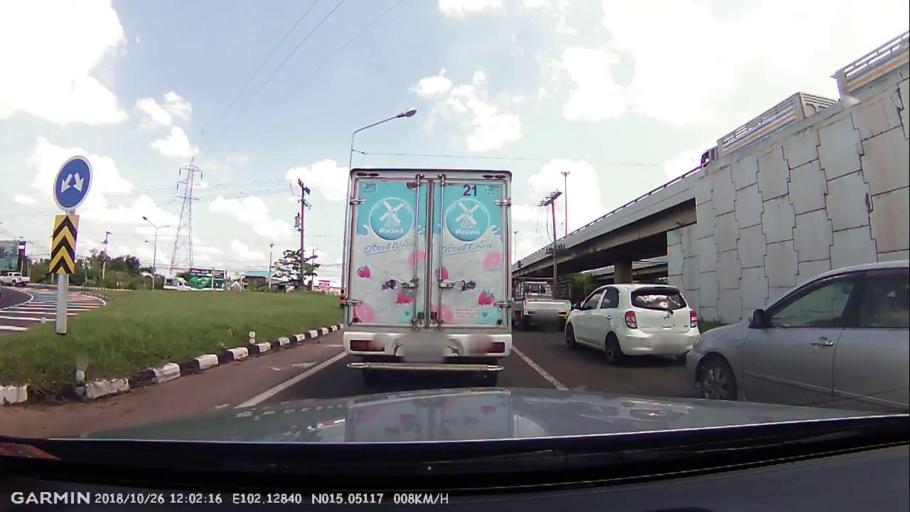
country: TH
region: Nakhon Ratchasima
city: Nakhon Ratchasima
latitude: 15.0511
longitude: 102.1282
